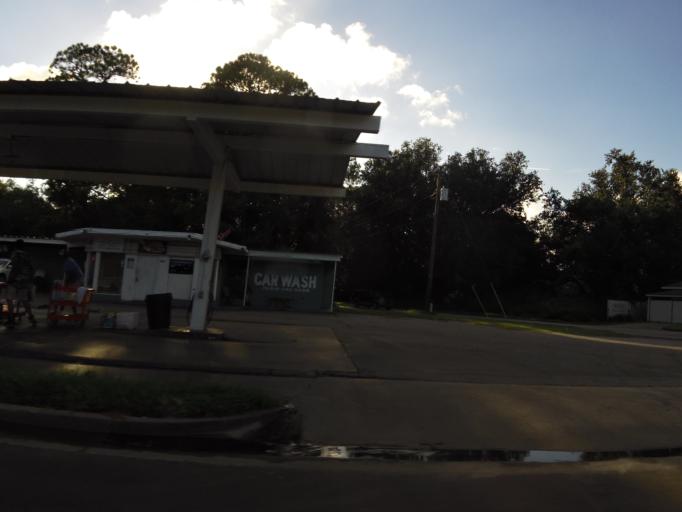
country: US
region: Georgia
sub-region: Glynn County
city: Brunswick
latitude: 31.1796
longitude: -81.4898
